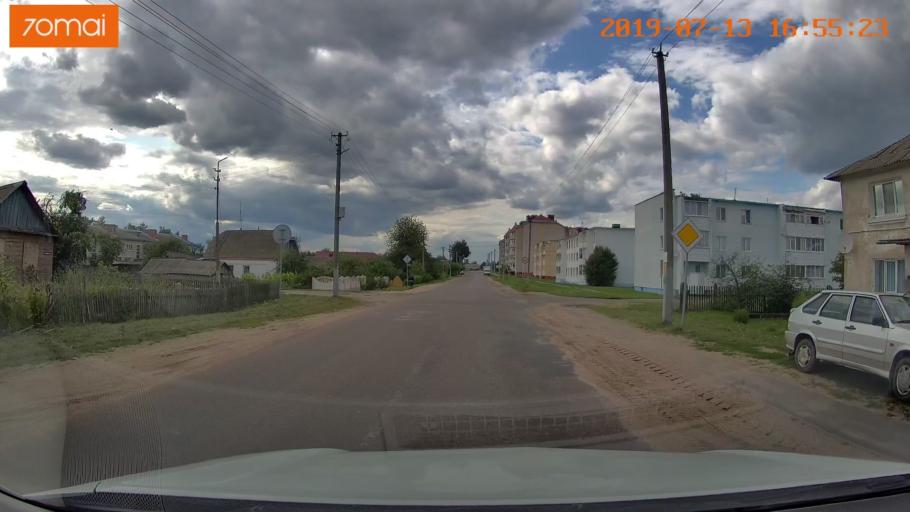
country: BY
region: Mogilev
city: Kirawsk
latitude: 53.2674
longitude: 29.4678
